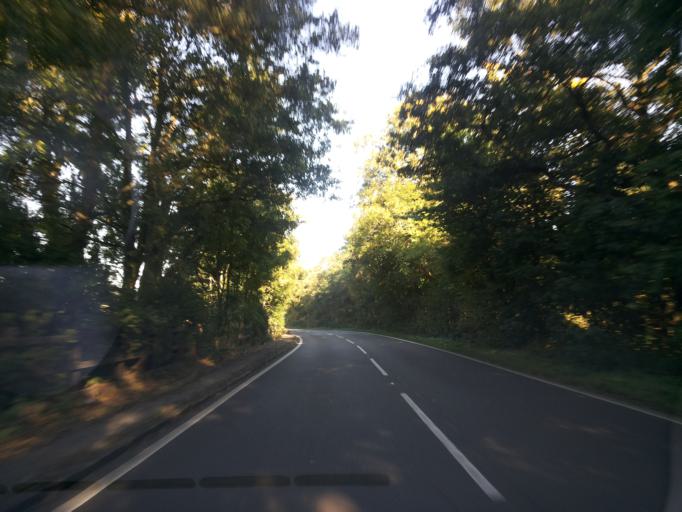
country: GB
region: England
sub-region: Derbyshire
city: Bakewell
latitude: 53.2405
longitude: -1.6359
